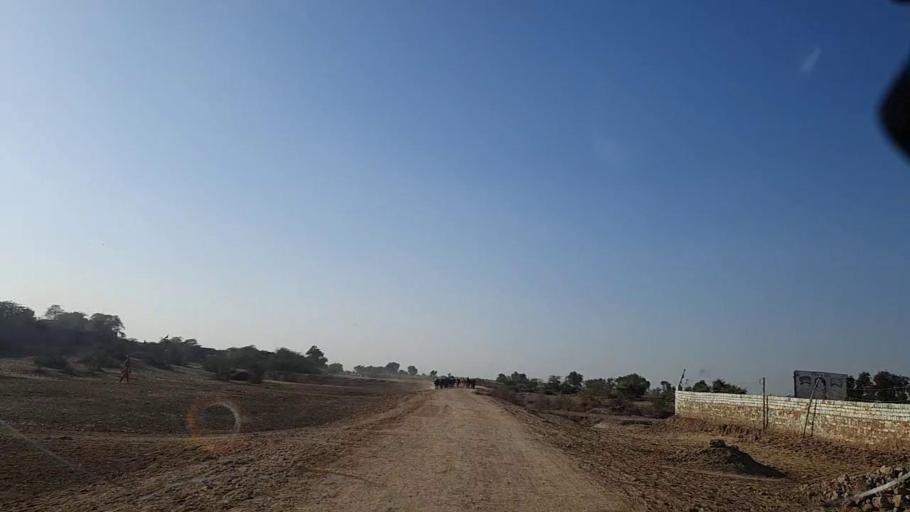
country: PK
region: Sindh
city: Khanpur
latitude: 27.7693
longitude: 69.2930
